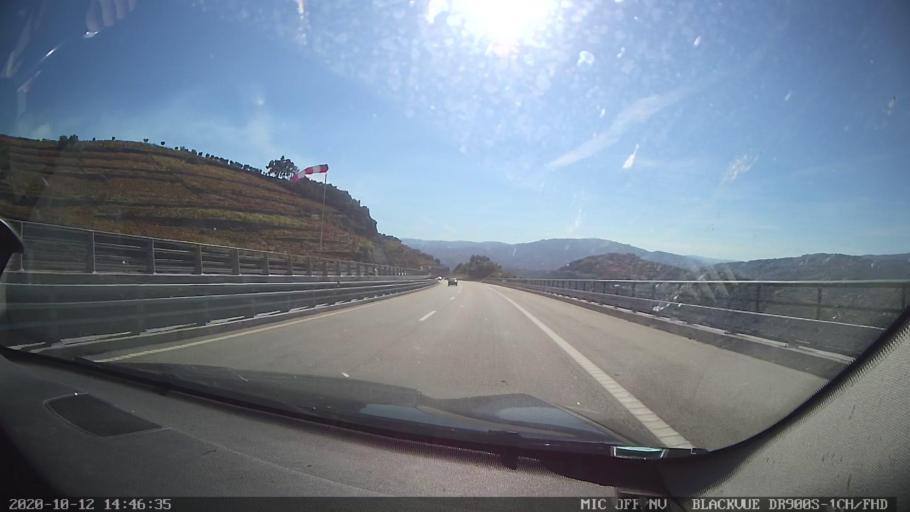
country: PT
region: Vila Real
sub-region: Santa Marta de Penaguiao
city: Santa Marta de Penaguiao
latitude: 41.2030
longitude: -7.7454
